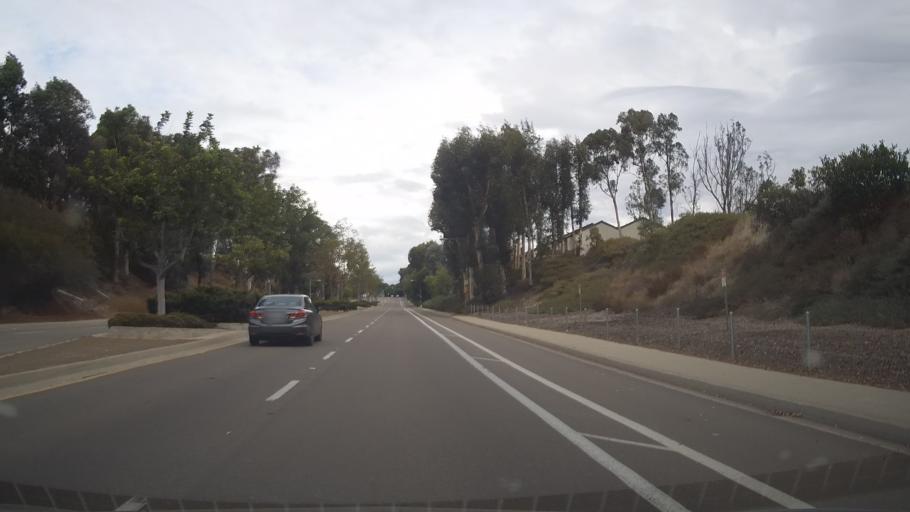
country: US
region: California
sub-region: San Diego County
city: La Mesa
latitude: 32.8341
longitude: -117.1008
